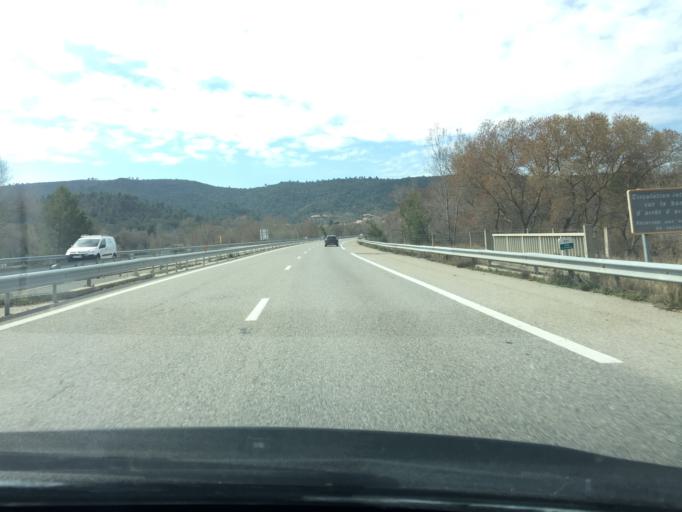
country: FR
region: Provence-Alpes-Cote d'Azur
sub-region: Departement du Vaucluse
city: Beaumont-de-Pertuis
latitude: 43.6927
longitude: 5.7207
